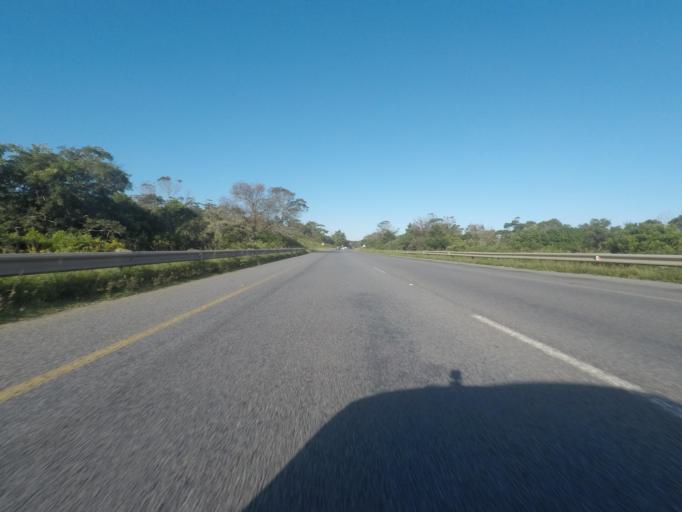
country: ZA
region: Eastern Cape
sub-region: Buffalo City Metropolitan Municipality
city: East London
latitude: -33.0615
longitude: 27.7874
